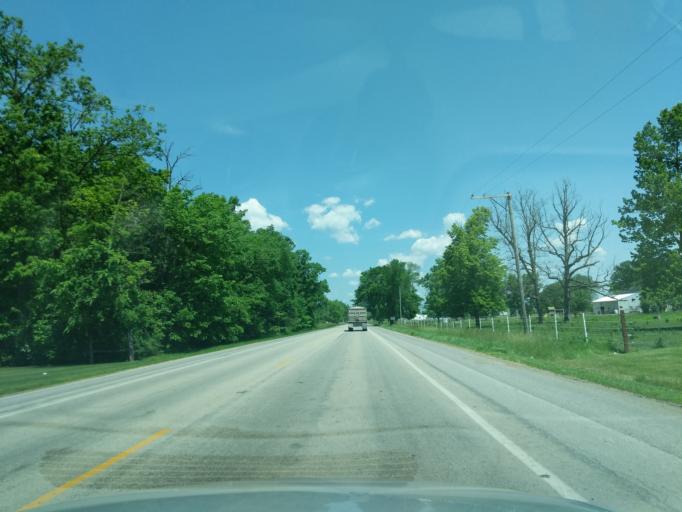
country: US
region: Indiana
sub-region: LaGrange County
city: Topeka
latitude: 41.5682
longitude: -85.5785
